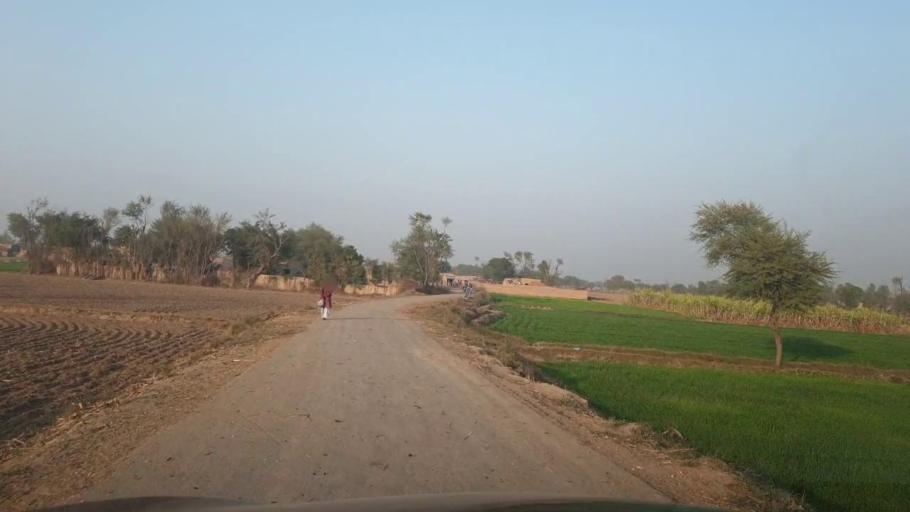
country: PK
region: Sindh
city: Ubauro
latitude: 28.3277
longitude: 69.7774
